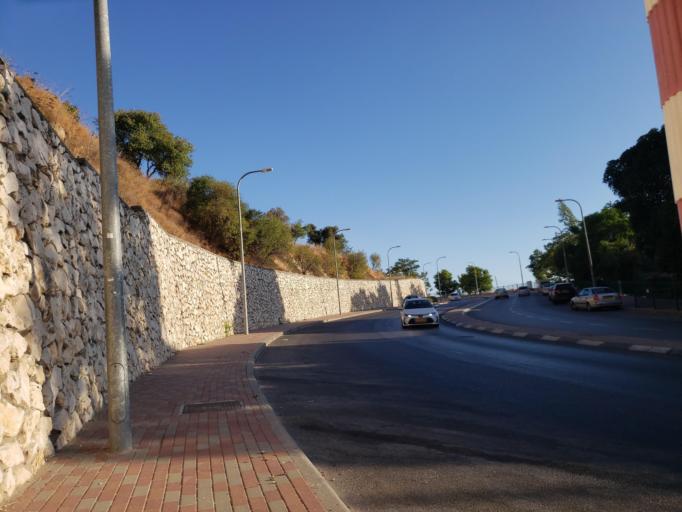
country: IL
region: Northern District
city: Safed
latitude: 32.9628
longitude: 35.4903
